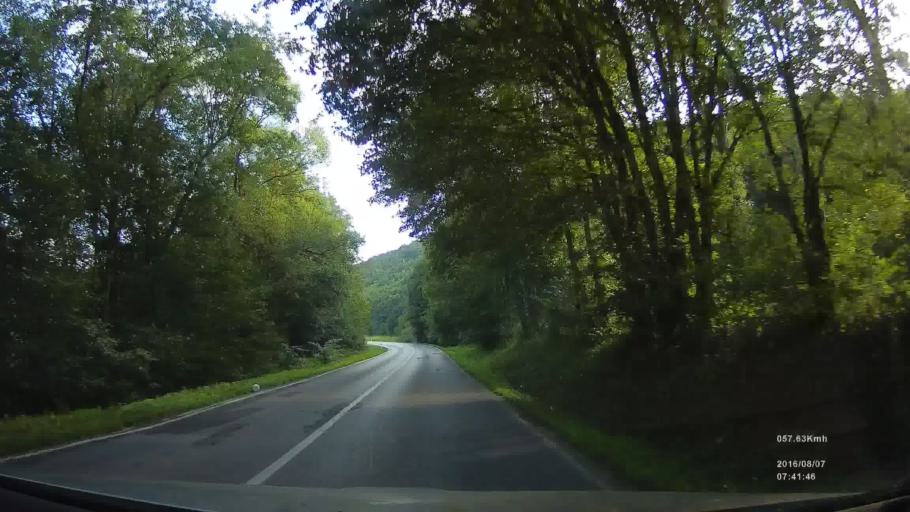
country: SK
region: Presovsky
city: Stropkov
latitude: 49.2562
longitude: 21.6920
